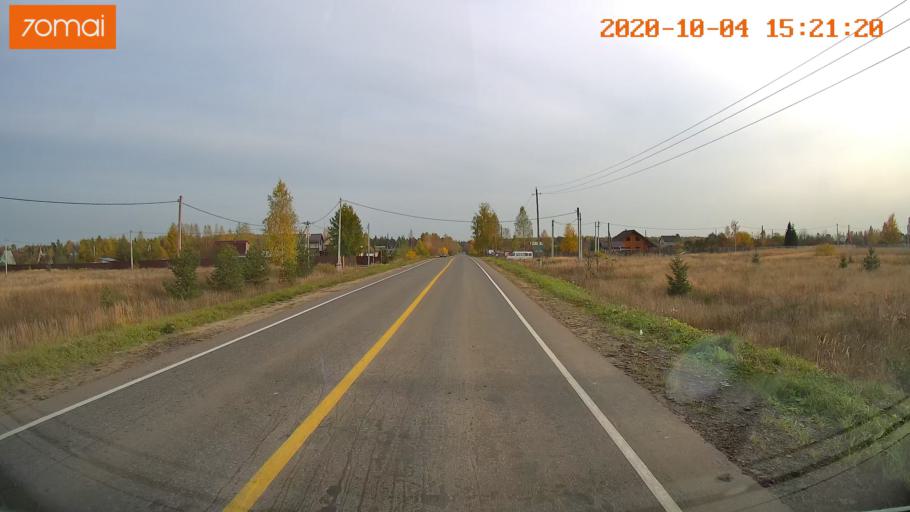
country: RU
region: Ivanovo
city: Bogorodskoye
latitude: 57.0869
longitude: 40.9216
